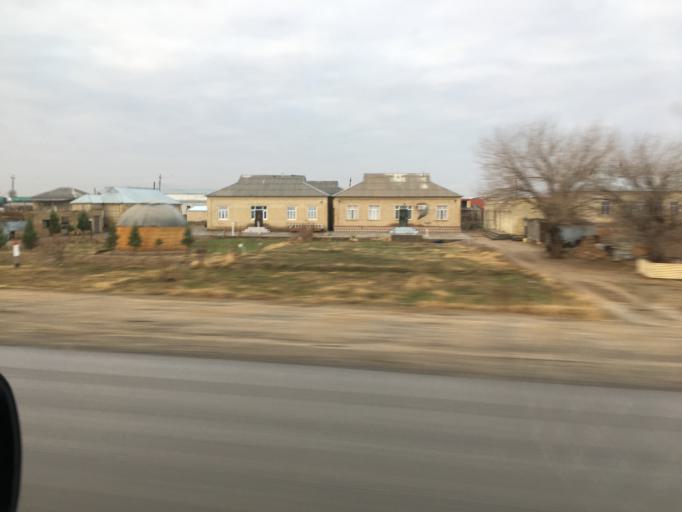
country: TM
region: Mary
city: Mary
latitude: 37.5390
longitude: 61.8799
